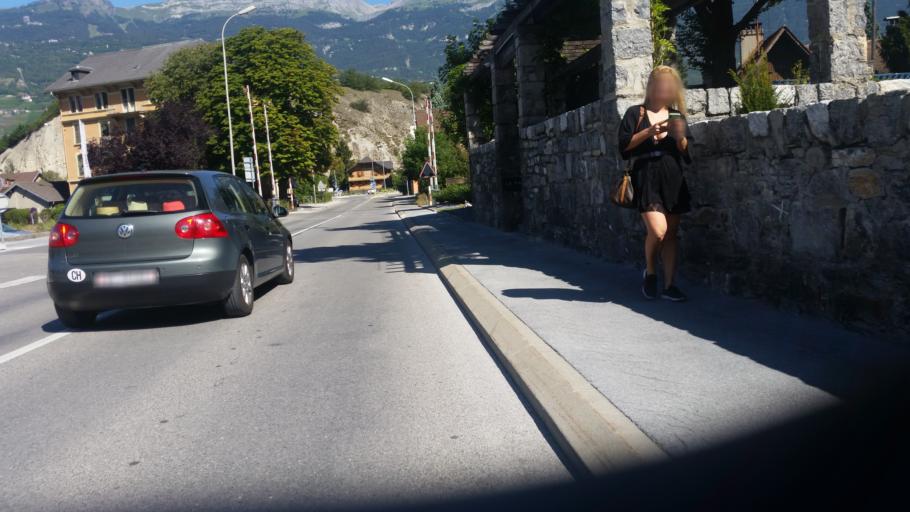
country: CH
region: Valais
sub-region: Sierre District
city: Chippis
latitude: 46.2832
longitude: 7.5401
